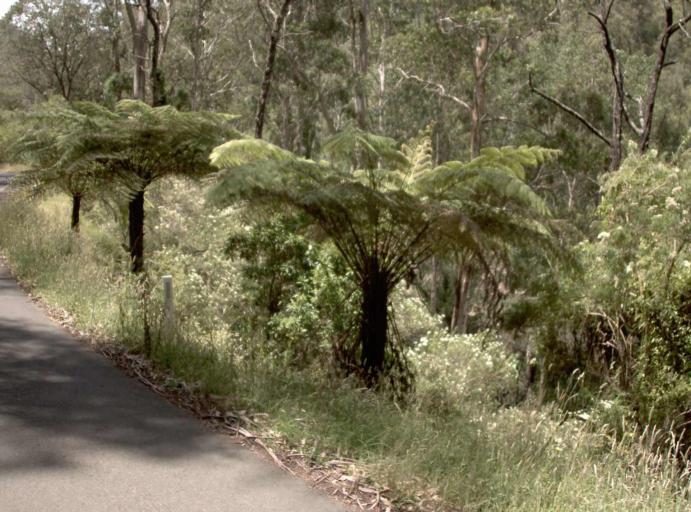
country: AU
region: Victoria
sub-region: Latrobe
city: Traralgon
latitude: -37.9531
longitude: 146.4260
